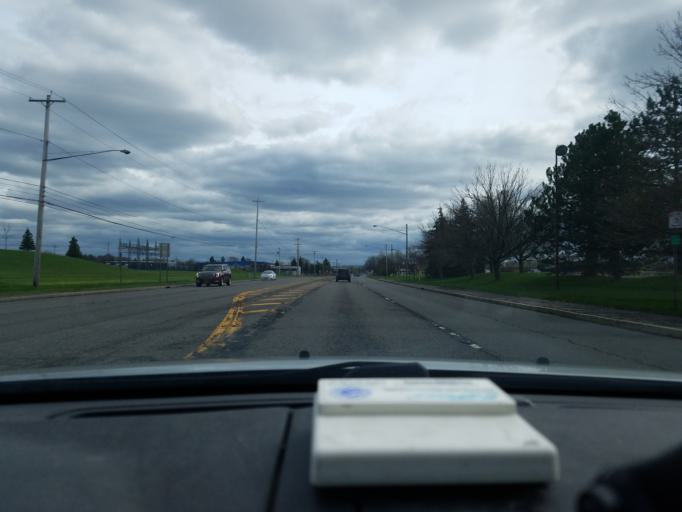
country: US
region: New York
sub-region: Onondaga County
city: East Syracuse
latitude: 43.0838
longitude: -76.0898
